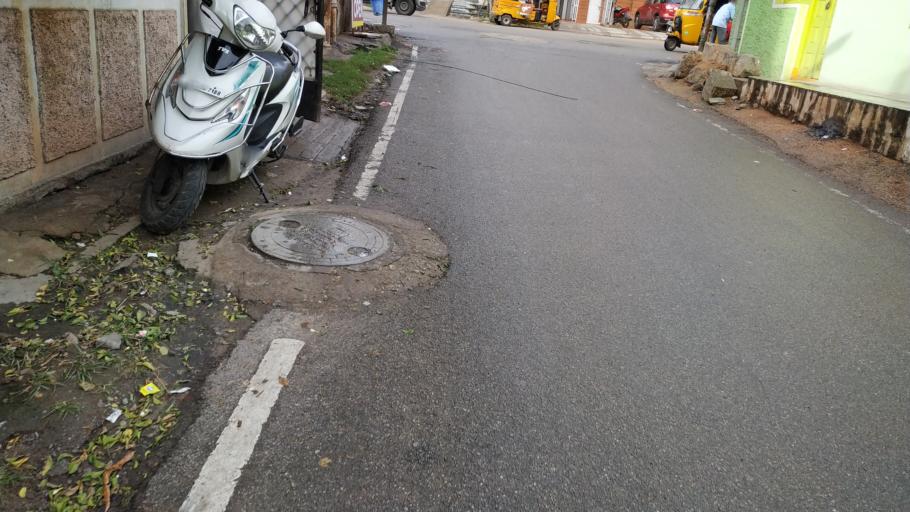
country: IN
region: Telangana
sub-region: Hyderabad
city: Malkajgiri
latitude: 17.4234
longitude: 78.5162
